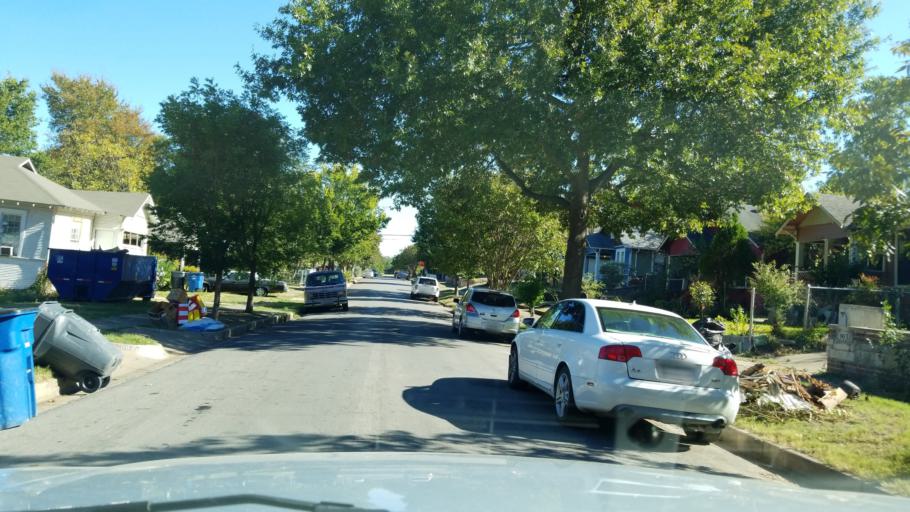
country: US
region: Texas
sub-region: Dallas County
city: Highland Park
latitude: 32.8009
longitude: -96.7446
